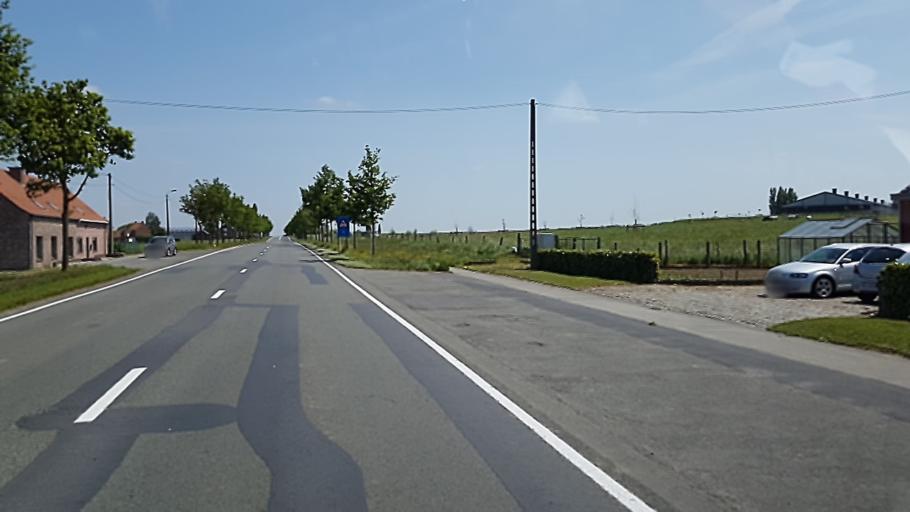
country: BE
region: Flanders
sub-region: Provincie West-Vlaanderen
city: Wervik
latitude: 50.8221
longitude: 3.0336
